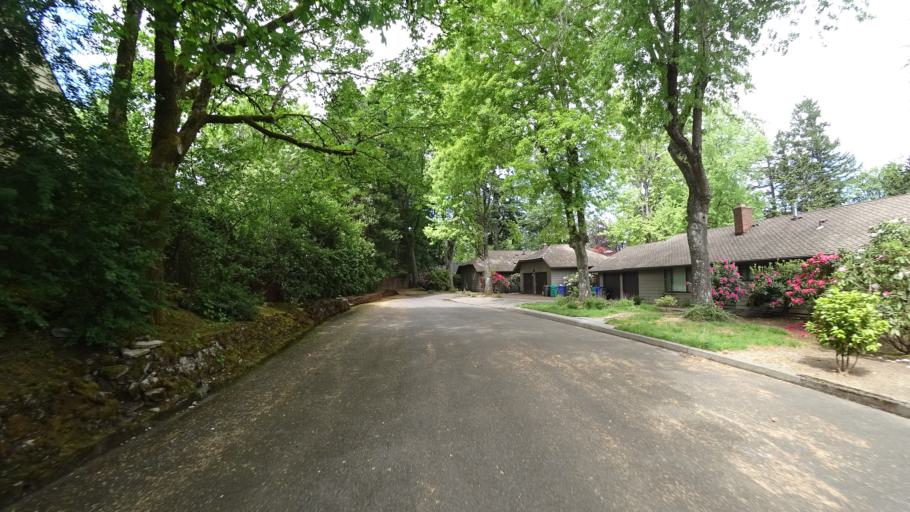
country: US
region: Oregon
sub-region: Washington County
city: Metzger
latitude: 45.4540
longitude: -122.7276
